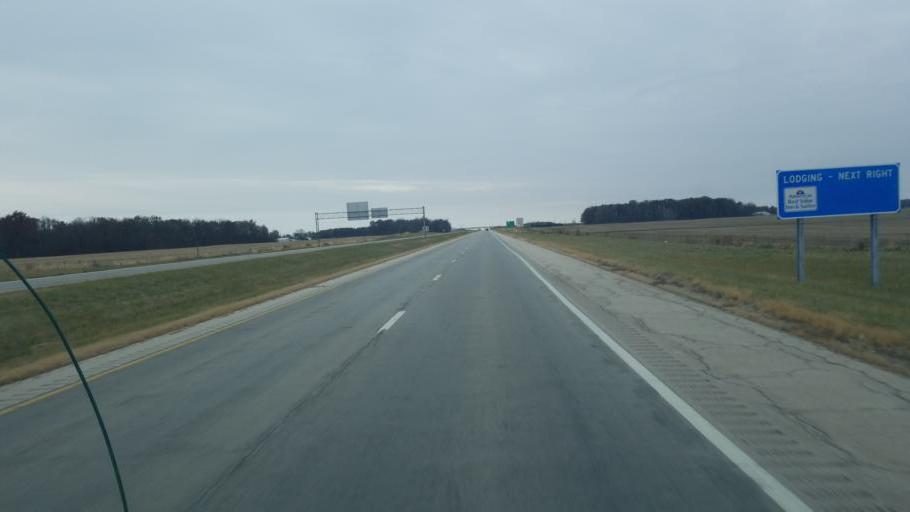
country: US
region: Ohio
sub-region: Auglaize County
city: Saint Marys
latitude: 40.5574
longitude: -84.4259
